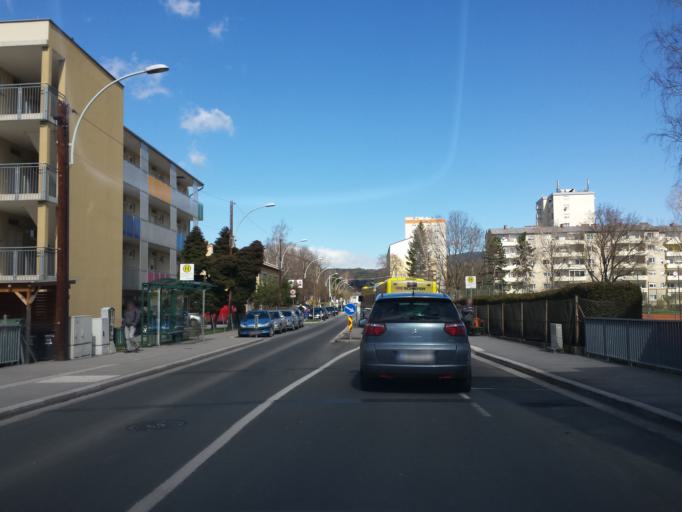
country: AT
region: Styria
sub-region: Graz Stadt
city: Goesting
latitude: 47.0931
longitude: 15.4137
